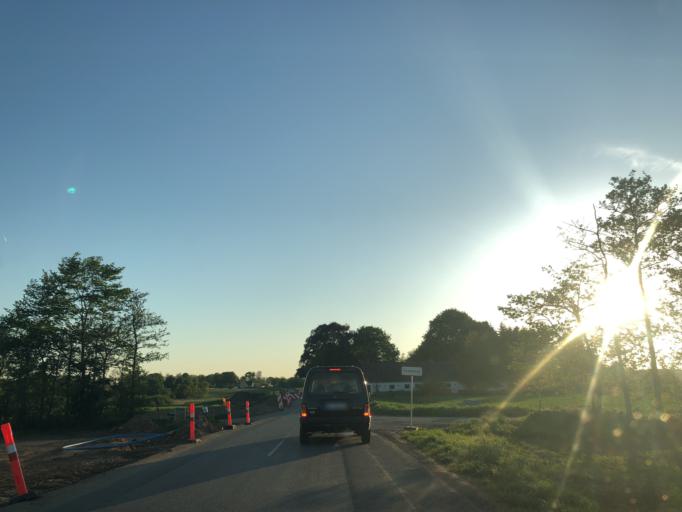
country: DK
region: Zealand
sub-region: Ringsted Kommune
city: Ringsted
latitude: 55.4073
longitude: 11.8690
